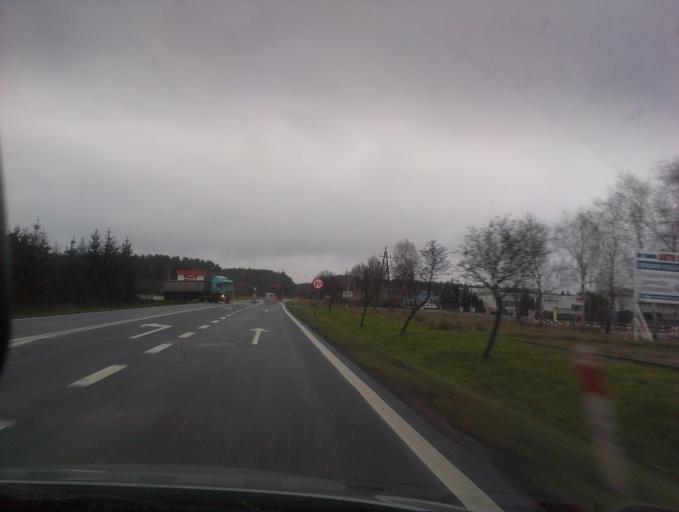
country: PL
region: Greater Poland Voivodeship
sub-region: Powiat chodzieski
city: Budzyn
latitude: 52.9016
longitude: 16.9704
